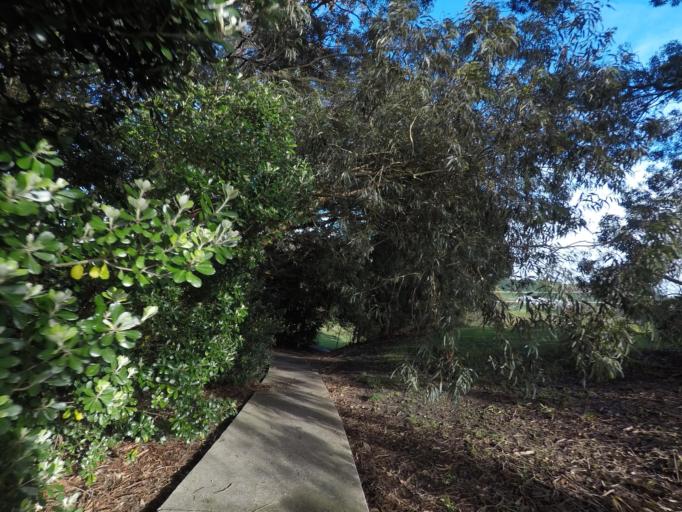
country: NZ
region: Auckland
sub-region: Auckland
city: Warkworth
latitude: -36.4221
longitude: 174.7215
